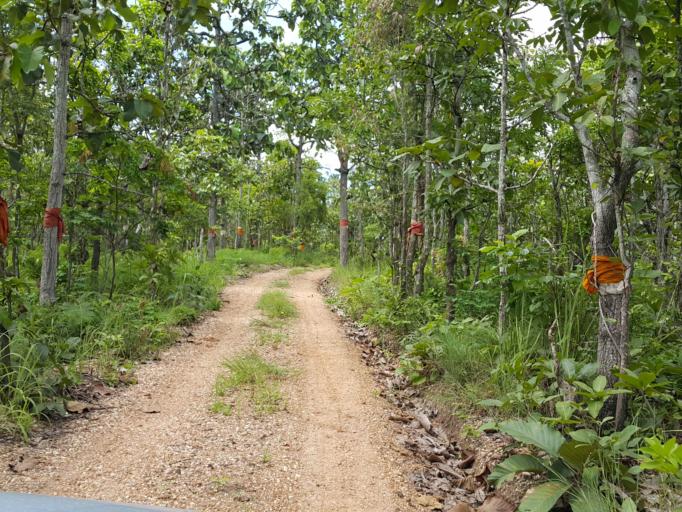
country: TH
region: Chiang Mai
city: Mae Taeng
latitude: 18.9521
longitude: 98.9118
